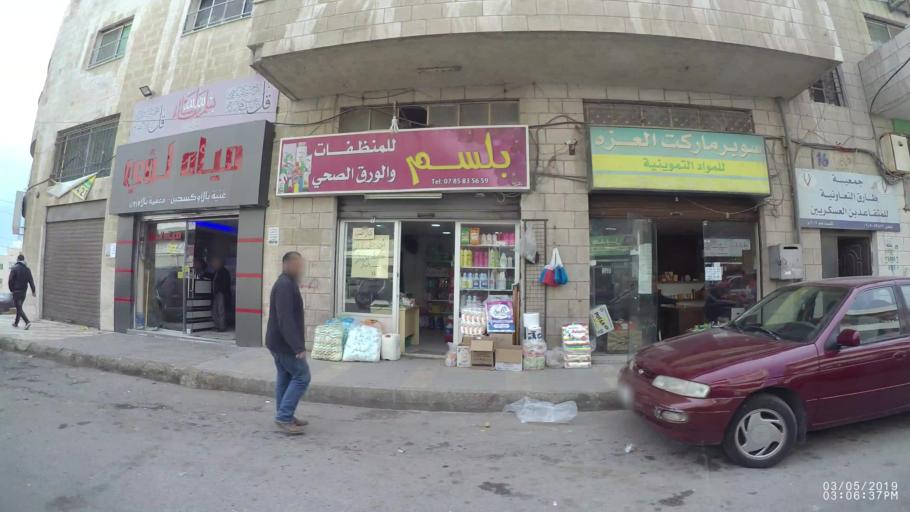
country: JO
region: Amman
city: Amman
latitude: 31.9988
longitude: 35.9460
